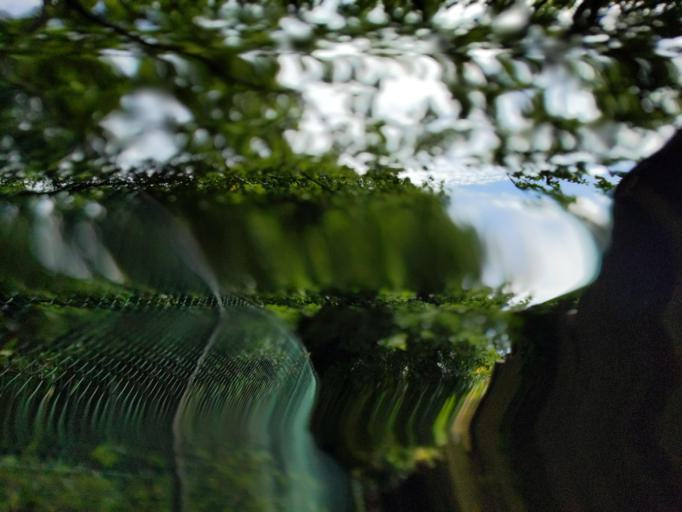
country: GB
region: England
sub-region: Greater London
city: West Wickham
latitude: 51.3767
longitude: 0.0003
